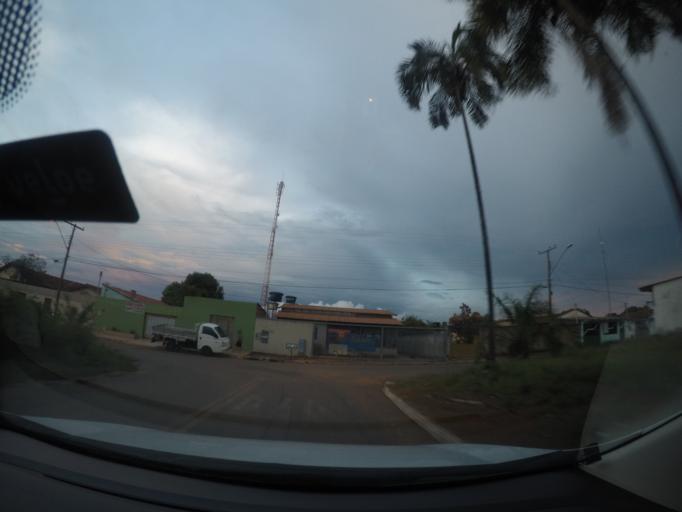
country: BR
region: Goias
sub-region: Goiania
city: Goiania
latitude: -16.7174
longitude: -49.3728
